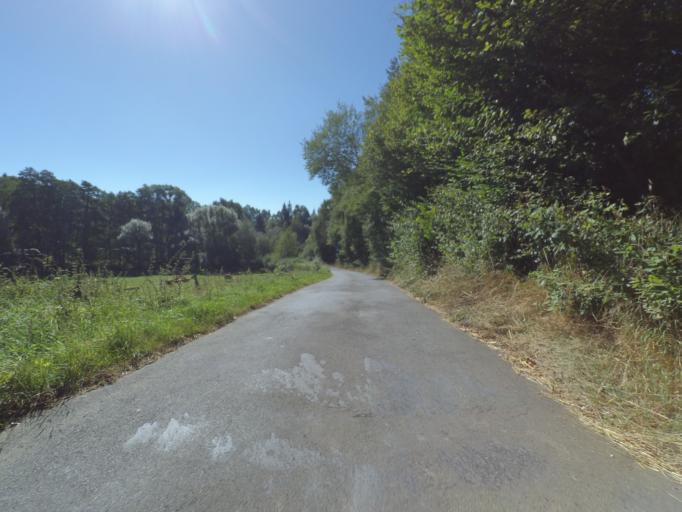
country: DE
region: Rheinland-Pfalz
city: Schonbach
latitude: 50.2013
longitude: 6.9547
